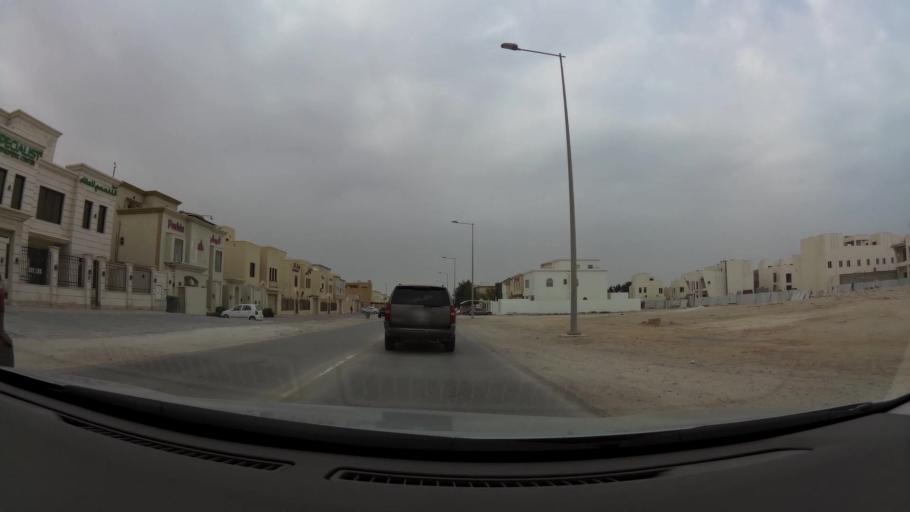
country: QA
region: Baladiyat ar Rayyan
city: Ar Rayyan
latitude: 25.3379
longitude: 51.4737
